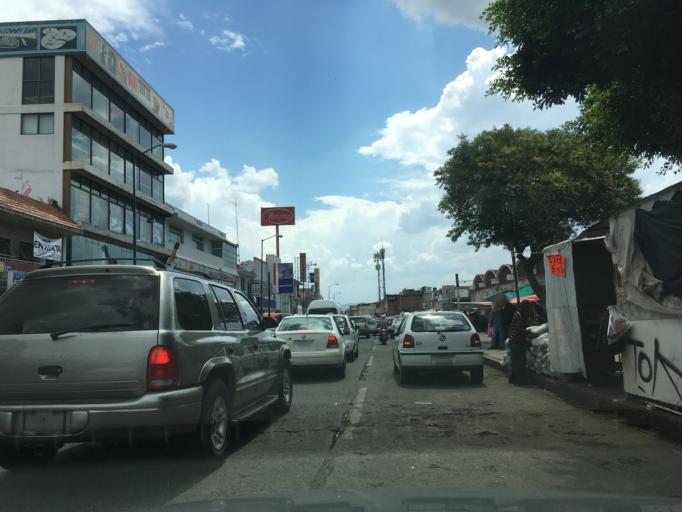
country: MX
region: Michoacan
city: Morelia
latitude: 19.6959
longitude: -101.1880
